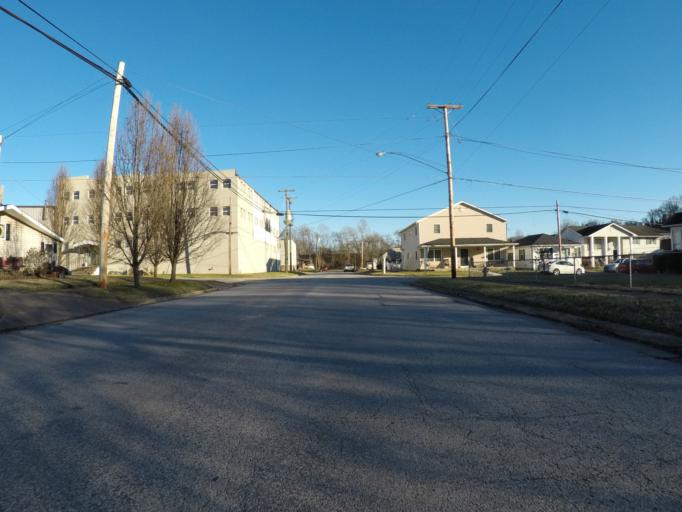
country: US
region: West Virginia
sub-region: Wayne County
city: Kenova
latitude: 38.3979
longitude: -82.5803
